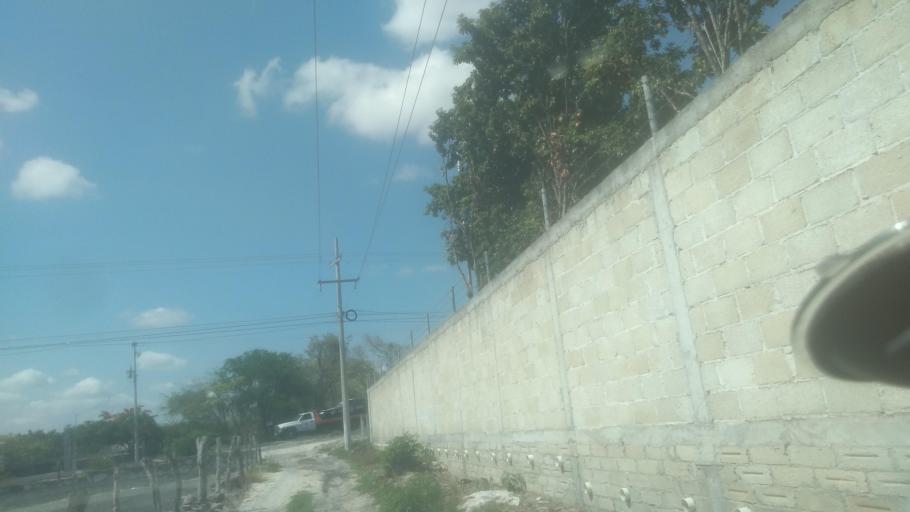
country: MX
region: Veracruz
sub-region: Emiliano Zapata
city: Plan del Rio
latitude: 19.3935
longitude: -96.6267
